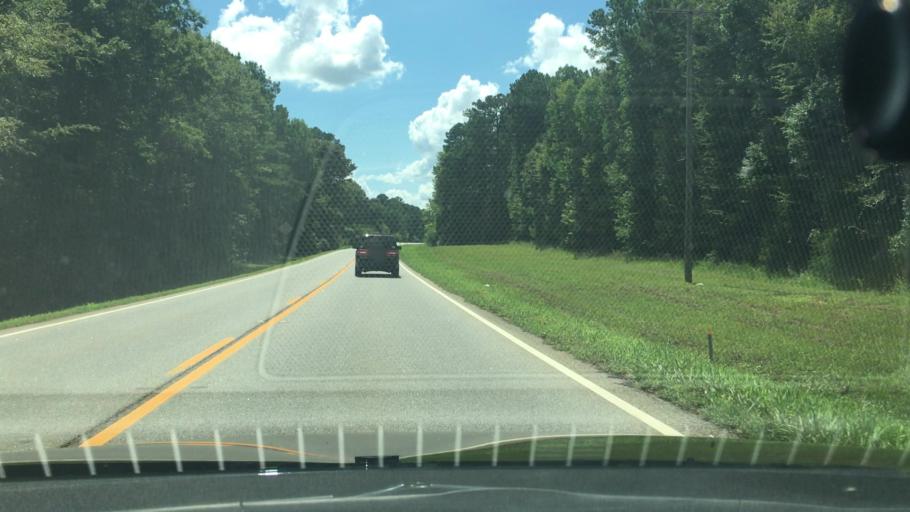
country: US
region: Georgia
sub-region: Putnam County
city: Eatonton
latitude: 33.3074
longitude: -83.4772
